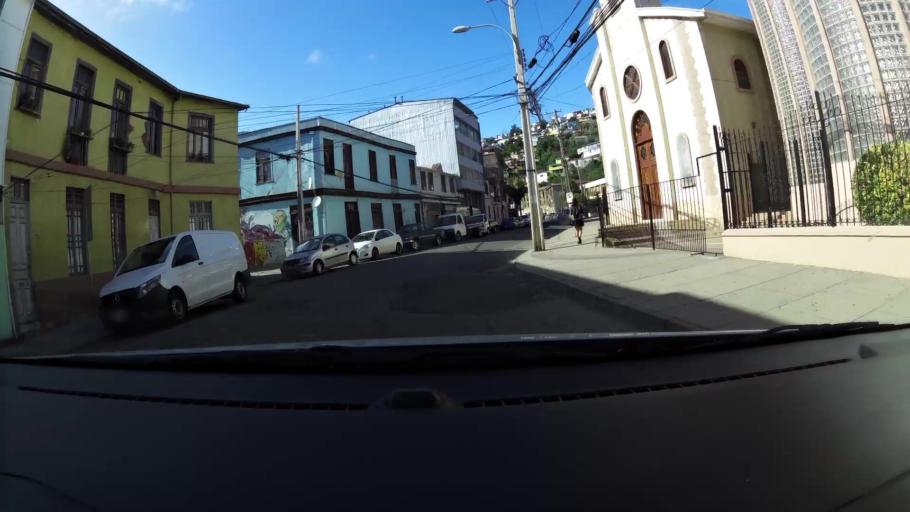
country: CL
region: Valparaiso
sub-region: Provincia de Valparaiso
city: Valparaiso
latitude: -33.0539
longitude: -71.6019
